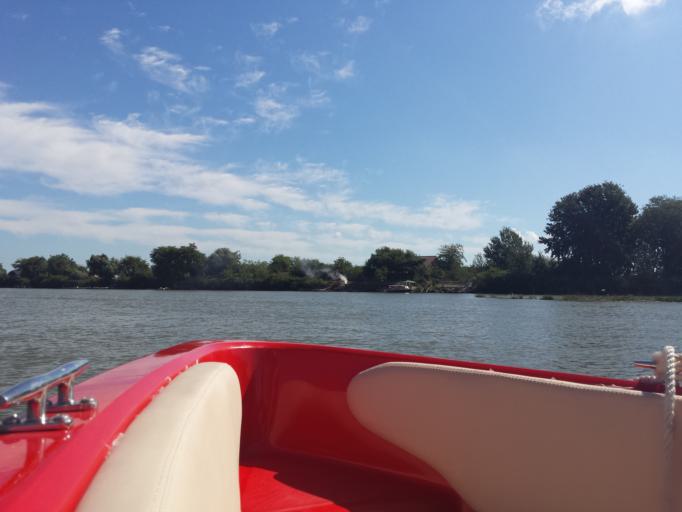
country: RO
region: Tulcea
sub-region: Comuna Crisan
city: Crisan
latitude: 45.2190
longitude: 29.2324
